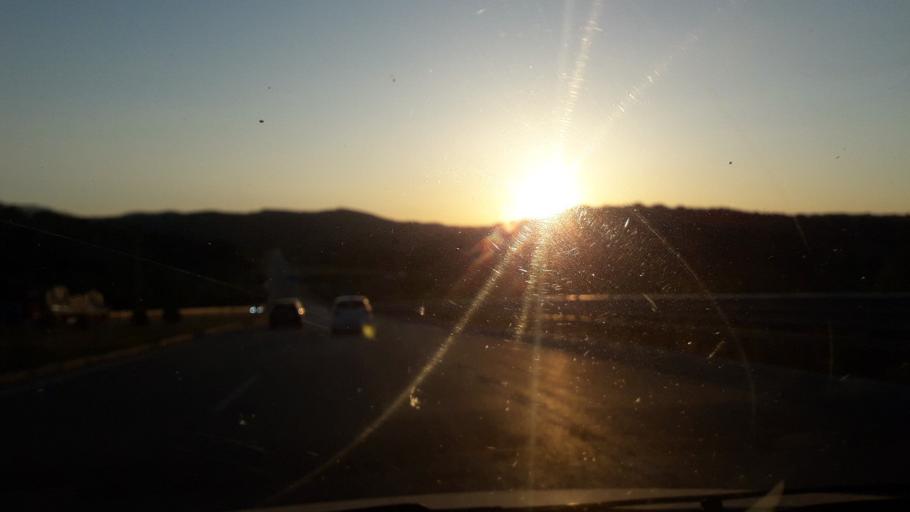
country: TR
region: Sinop
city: Kabali
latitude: 41.8572
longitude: 35.1049
